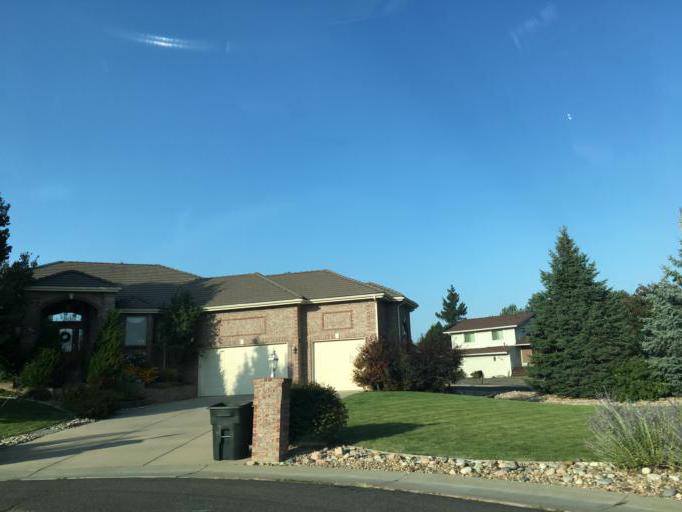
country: US
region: Colorado
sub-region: Jefferson County
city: Applewood
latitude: 39.7933
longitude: -105.1682
